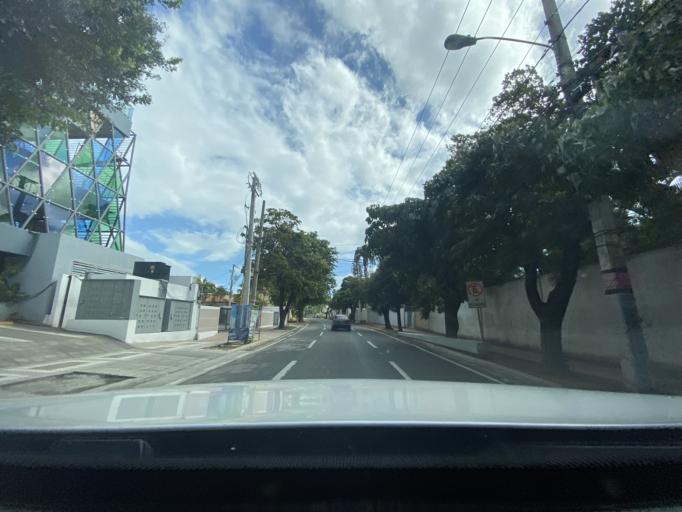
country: DO
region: Nacional
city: Ciudad Nueva
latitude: 18.4685
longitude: -69.9148
